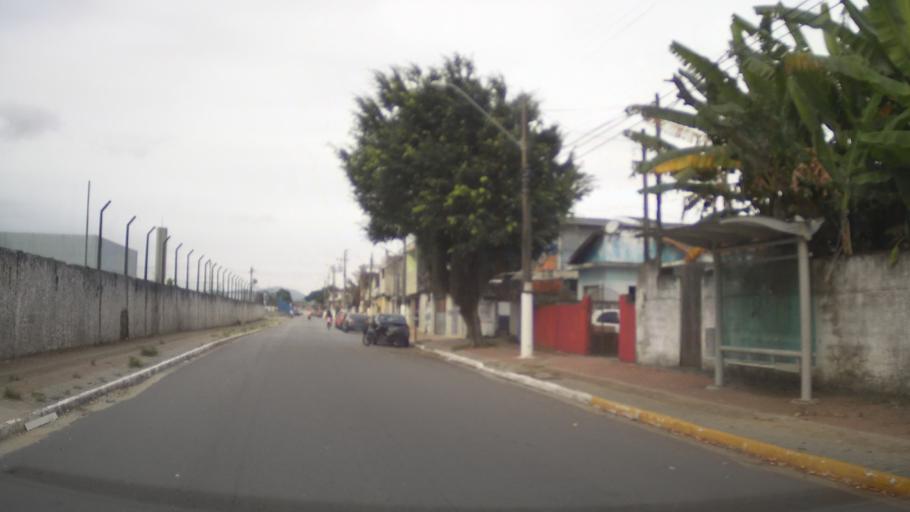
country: BR
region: Sao Paulo
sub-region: Praia Grande
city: Praia Grande
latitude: -24.0096
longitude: -46.4534
